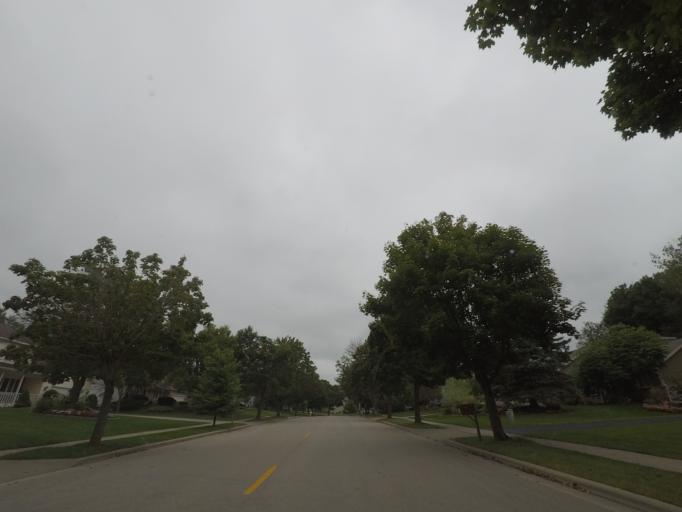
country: US
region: Wisconsin
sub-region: Dane County
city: Middleton
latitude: 43.0842
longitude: -89.5089
